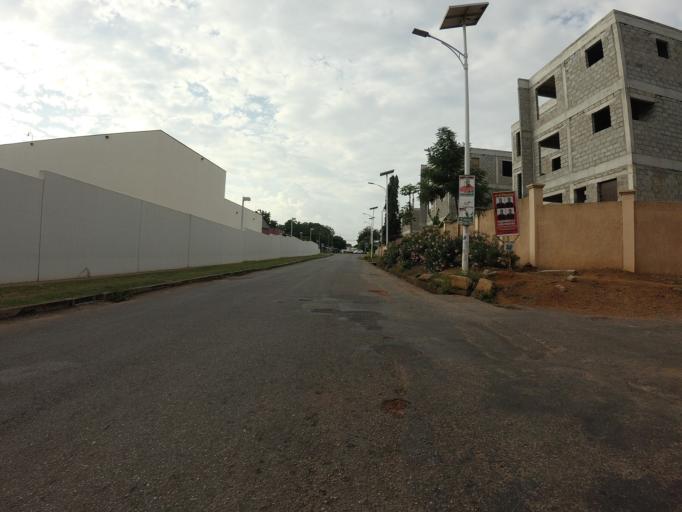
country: GH
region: Greater Accra
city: Accra
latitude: 5.5802
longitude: -0.1700
